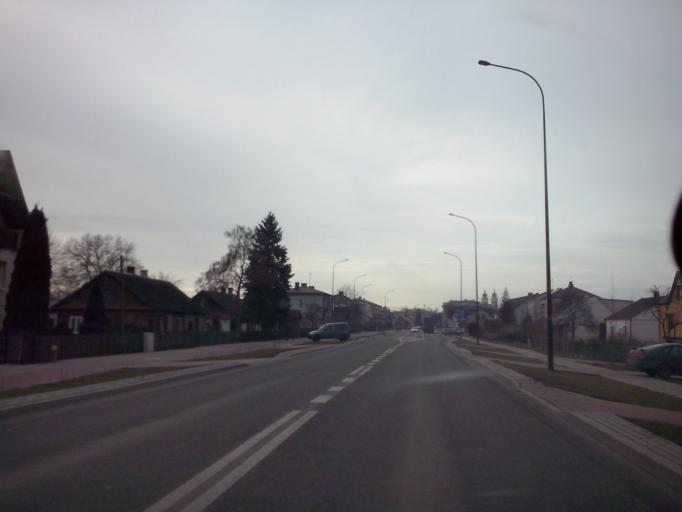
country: PL
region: Lublin Voivodeship
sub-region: Powiat bilgorajski
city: Bilgoraj
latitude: 50.5461
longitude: 22.7326
